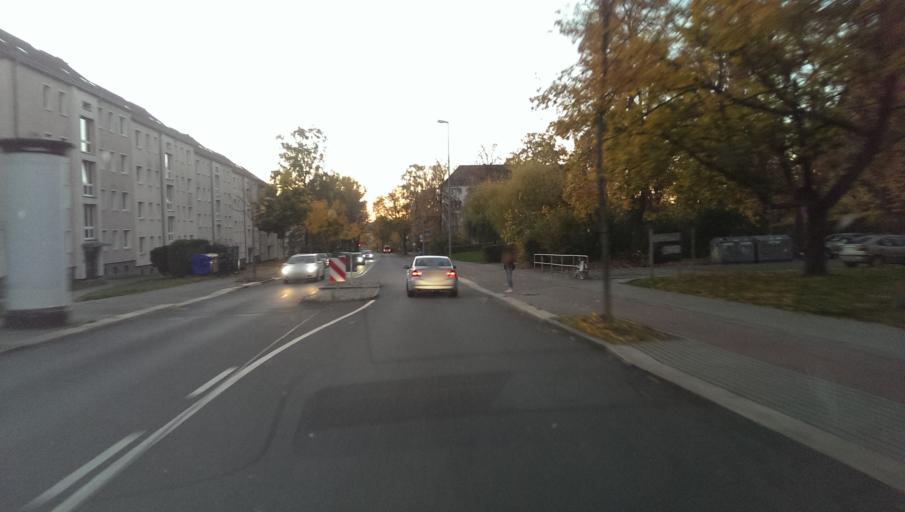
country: DE
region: Saxony
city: Chemnitz
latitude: 50.8215
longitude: 12.9379
